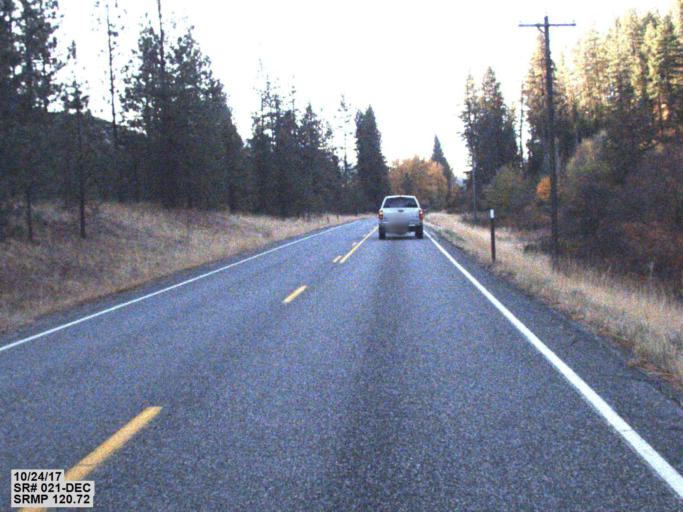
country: US
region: Washington
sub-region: Okanogan County
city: Coulee Dam
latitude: 48.1317
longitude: -118.6932
